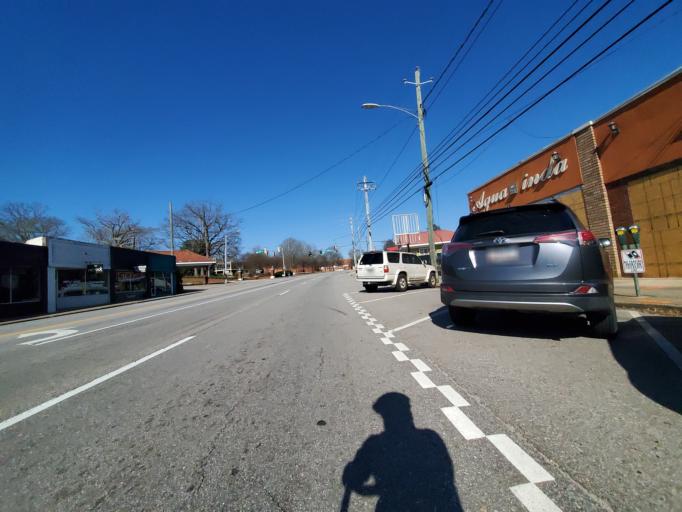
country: US
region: Georgia
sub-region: Clarke County
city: Athens
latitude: 33.9636
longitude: -83.4010
